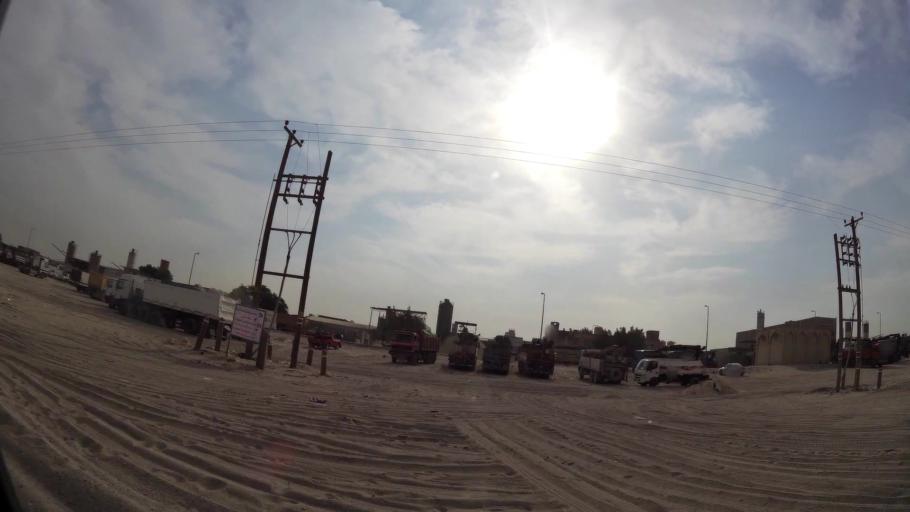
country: KW
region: Muhafazat al Jahra'
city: Al Jahra'
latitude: 29.3076
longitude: 47.7416
